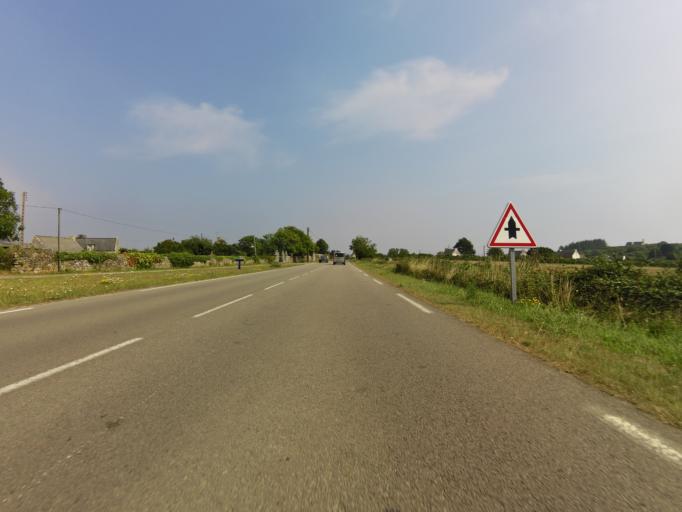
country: FR
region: Brittany
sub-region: Departement du Finistere
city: Plogoff
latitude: 48.0348
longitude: -4.6552
